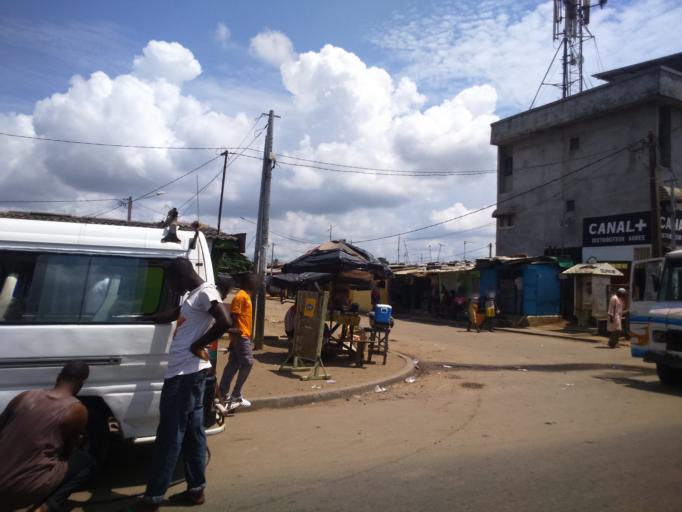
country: CI
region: Lagunes
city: Abidjan
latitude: 5.3501
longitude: -4.0875
